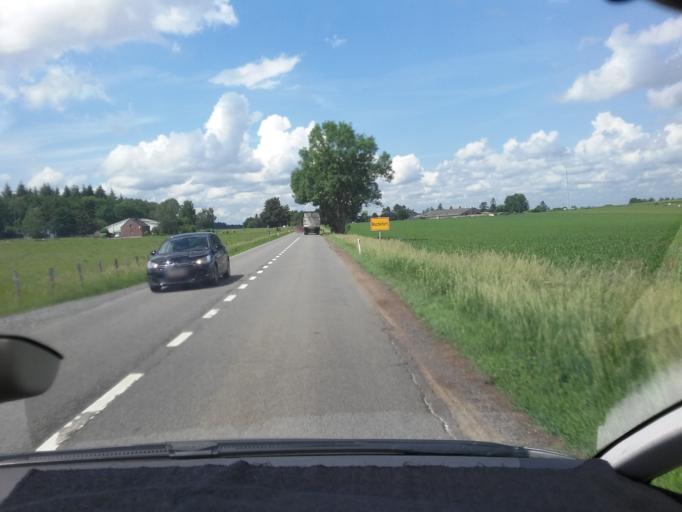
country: BE
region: Wallonia
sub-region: Province de Namur
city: Rochefort
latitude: 50.1341
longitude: 5.2312
